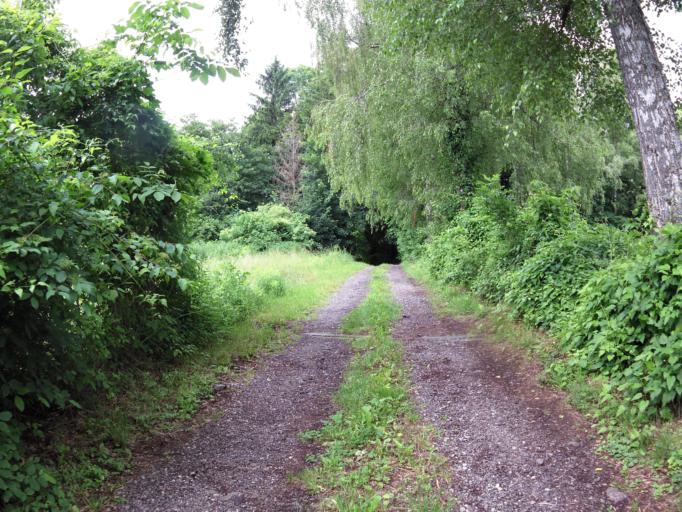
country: DE
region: Baden-Wuerttemberg
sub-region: Freiburg Region
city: Lahr
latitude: 48.3519
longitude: 7.8581
